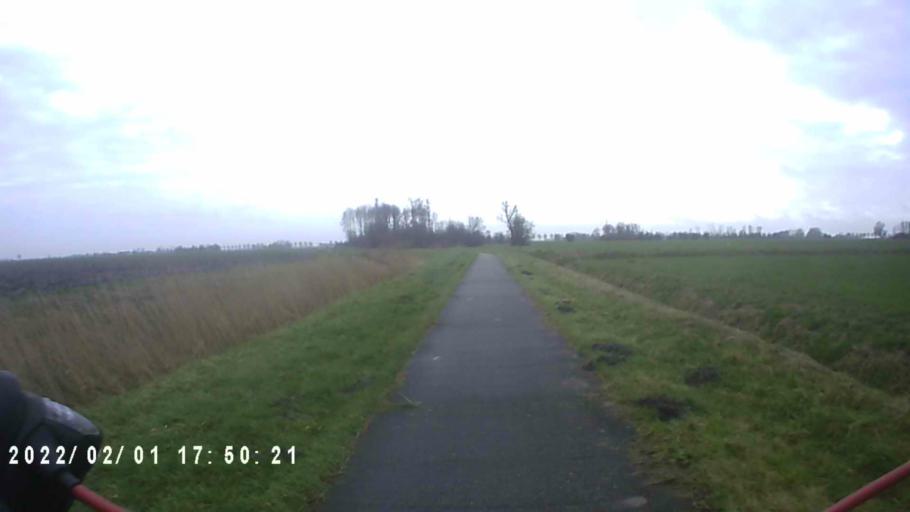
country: NL
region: Groningen
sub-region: Gemeente Zuidhorn
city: Oldehove
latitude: 53.3449
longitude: 6.4043
